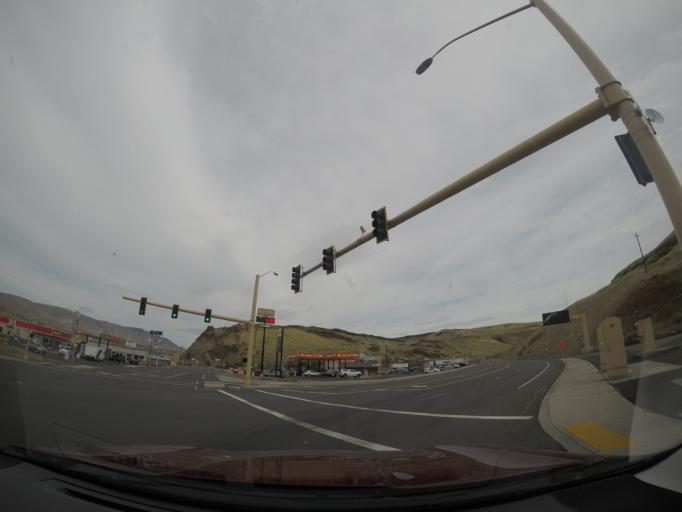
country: US
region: Washington
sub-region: Klickitat County
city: Goldendale
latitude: 45.6696
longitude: -120.8334
